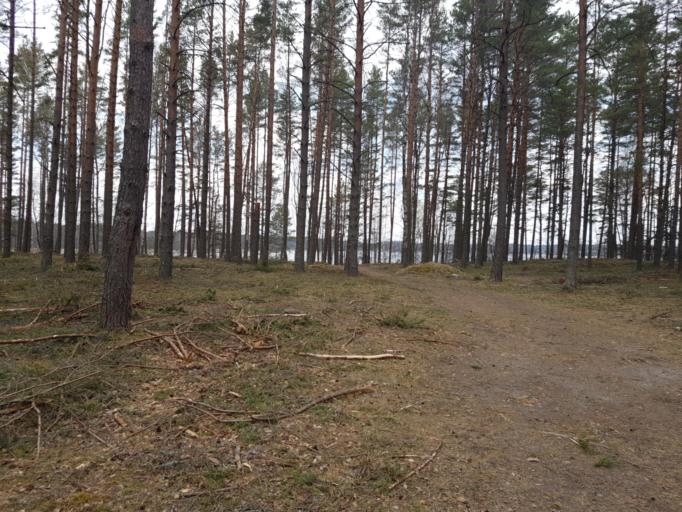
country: LV
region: Carnikava
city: Carnikava
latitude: 57.1728
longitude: 24.3547
